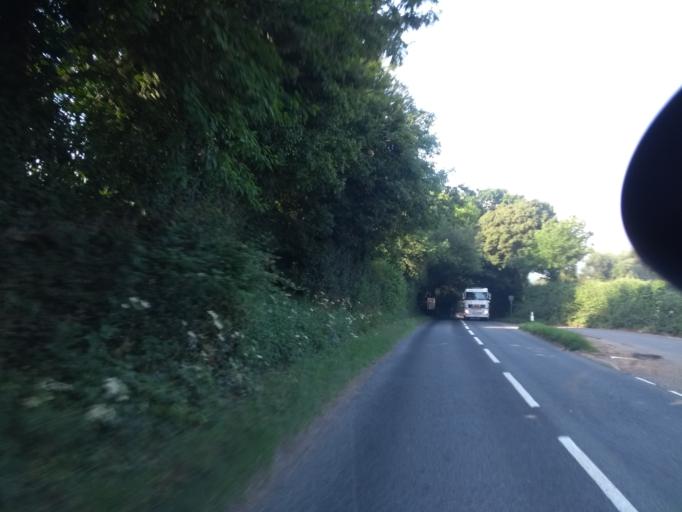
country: GB
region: England
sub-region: Somerset
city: Crewkerne
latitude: 50.8969
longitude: -2.7904
